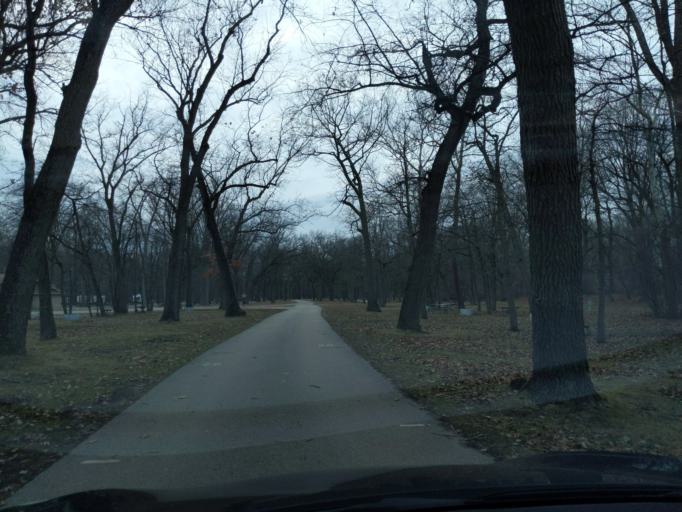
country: US
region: Michigan
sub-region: Bay County
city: Bay City
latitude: 43.6639
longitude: -83.8994
